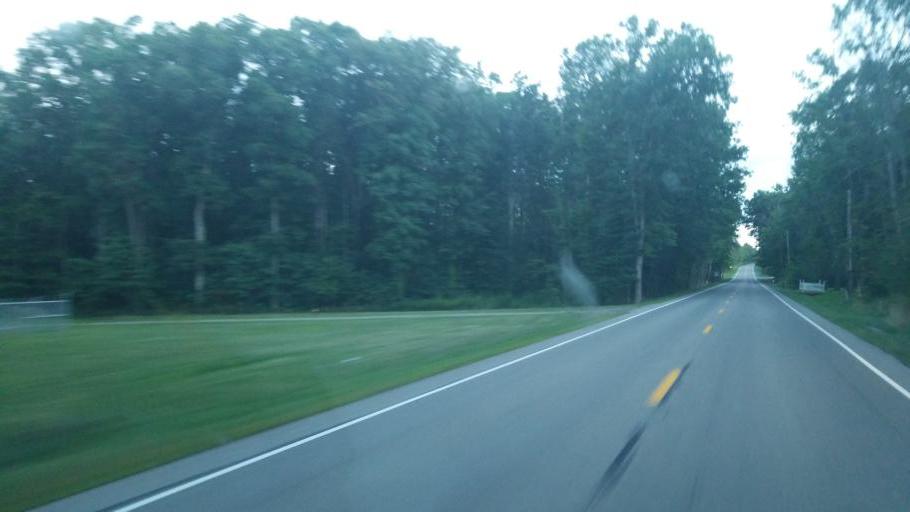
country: US
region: Pennsylvania
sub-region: Clarion County
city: Knox
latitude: 41.2036
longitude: -79.5433
